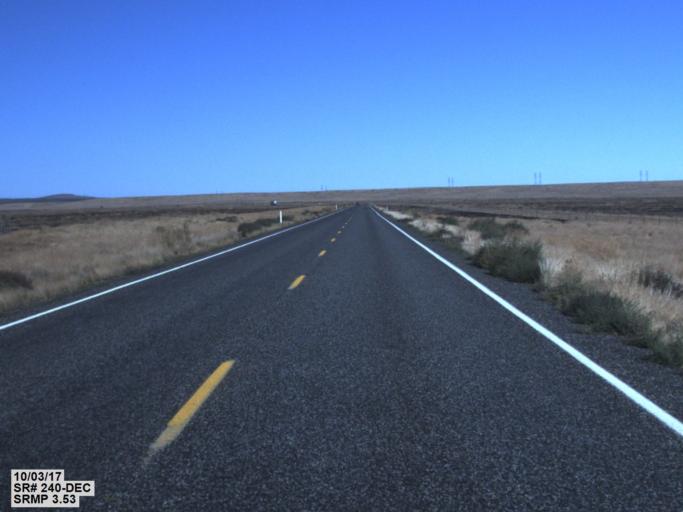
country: US
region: Washington
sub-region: Grant County
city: Desert Aire
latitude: 46.5380
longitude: -119.6853
